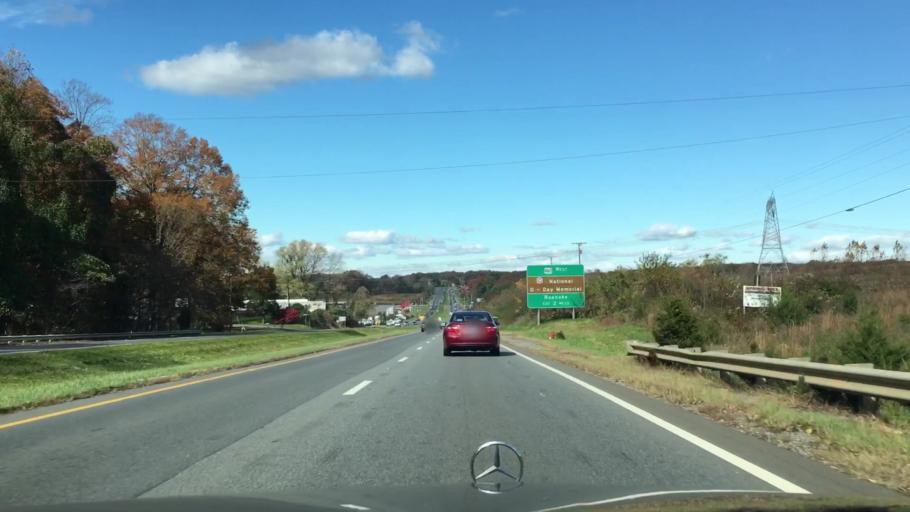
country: US
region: Virginia
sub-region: Campbell County
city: Timberlake
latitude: 37.3055
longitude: -79.1785
